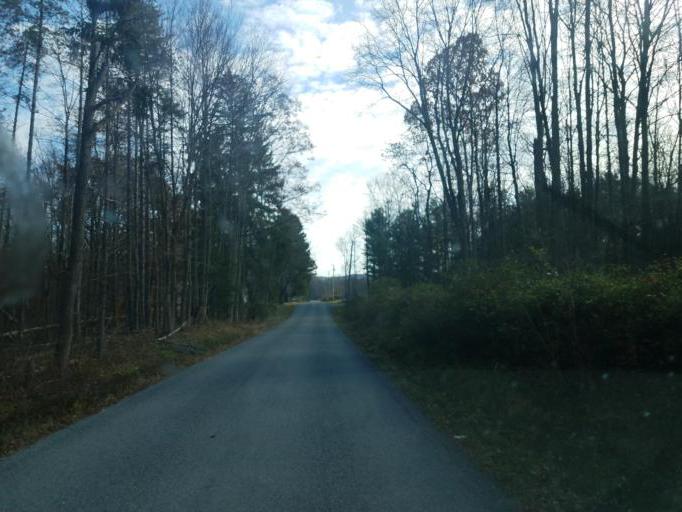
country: US
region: Ohio
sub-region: Richland County
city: Ontario
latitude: 40.7210
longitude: -82.6649
